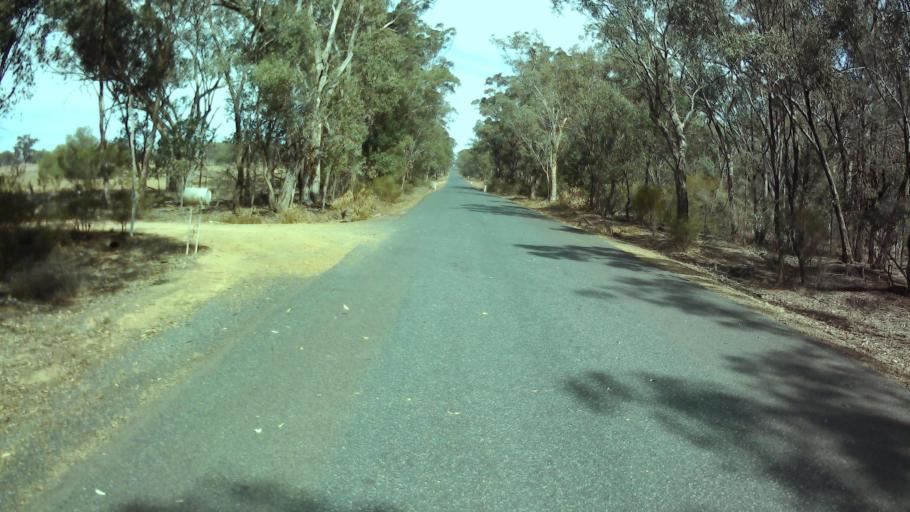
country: AU
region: New South Wales
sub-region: Weddin
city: Grenfell
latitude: -33.8077
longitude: 148.0576
